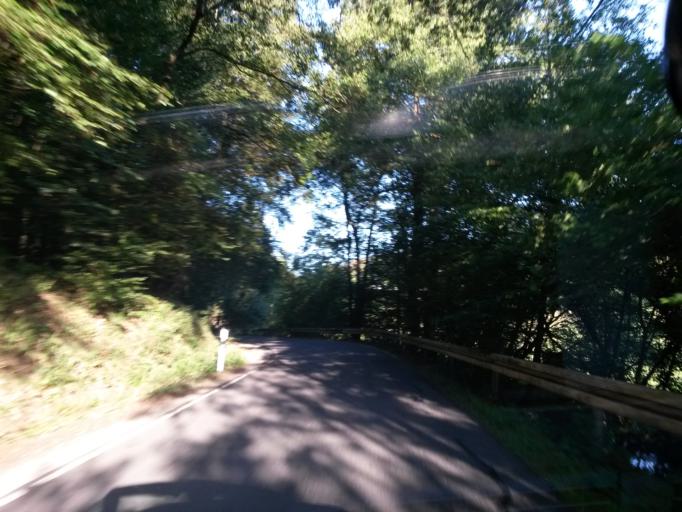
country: DE
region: North Rhine-Westphalia
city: Wipperfurth
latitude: 51.0755
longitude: 7.3760
